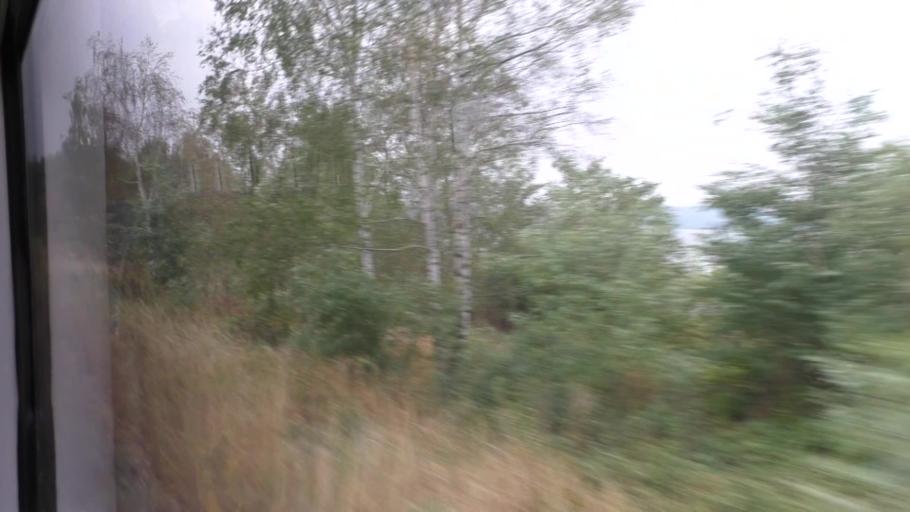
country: DE
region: Saxony
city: Goerlitz
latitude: 51.0913
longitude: 14.9756
